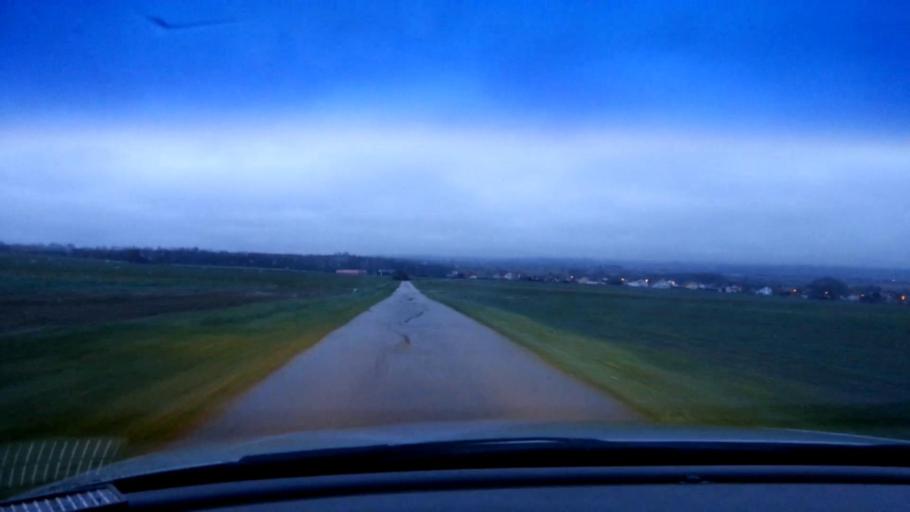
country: DE
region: Bavaria
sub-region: Upper Franconia
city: Gundelsheim
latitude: 49.9621
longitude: 10.9443
